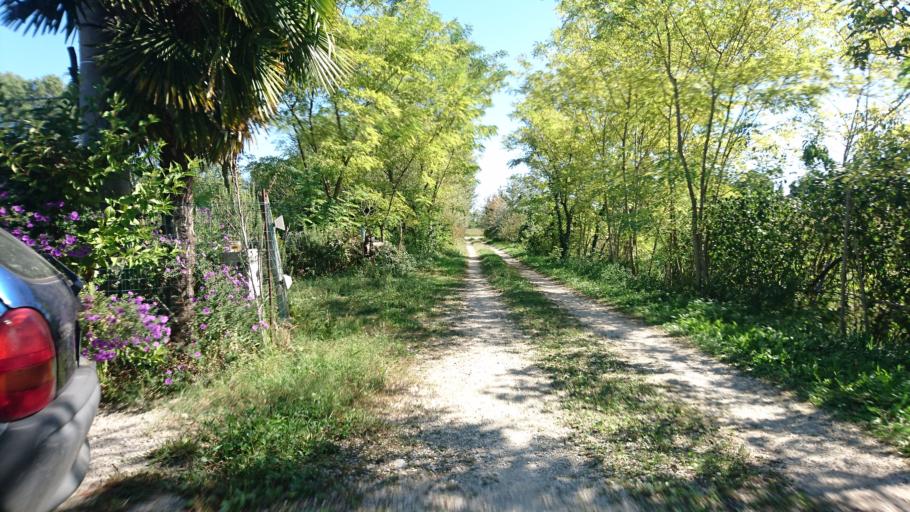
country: IT
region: Veneto
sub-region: Provincia di Venezia
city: Dolo
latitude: 45.4124
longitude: 12.0679
